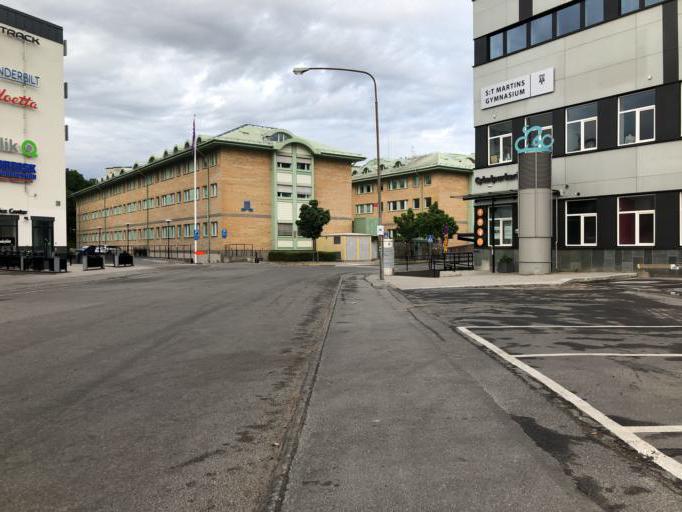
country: SE
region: Stockholm
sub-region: Solna Kommun
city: Rasunda
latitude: 59.3602
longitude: 17.9800
